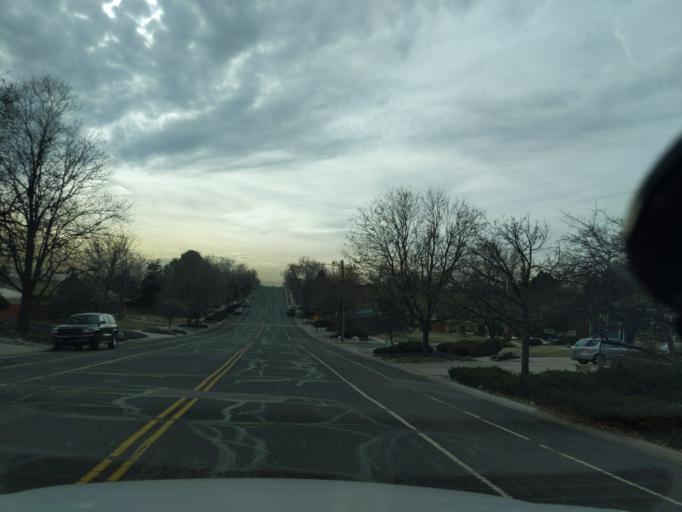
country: US
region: Colorado
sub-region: Adams County
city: Thornton
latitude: 39.8629
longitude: -104.9514
